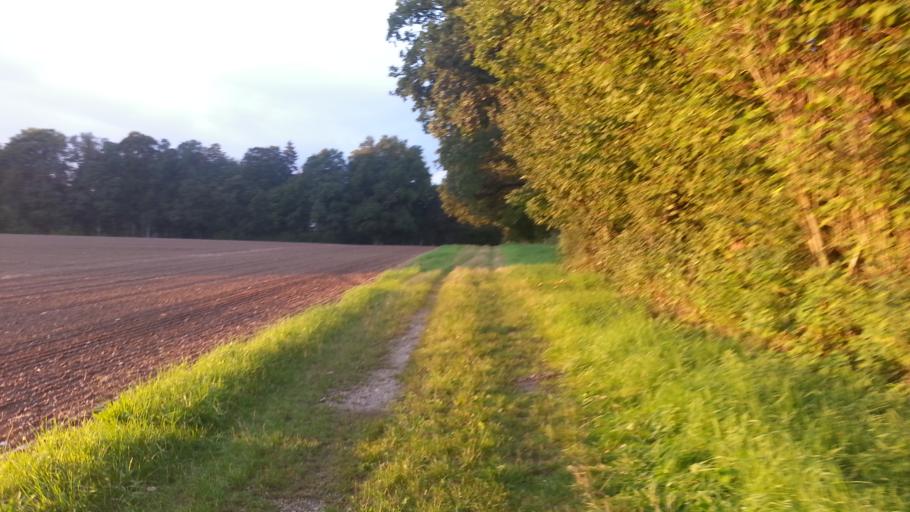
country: DE
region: Bavaria
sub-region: Upper Bavaria
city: Gilching
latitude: 48.1127
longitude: 11.3240
